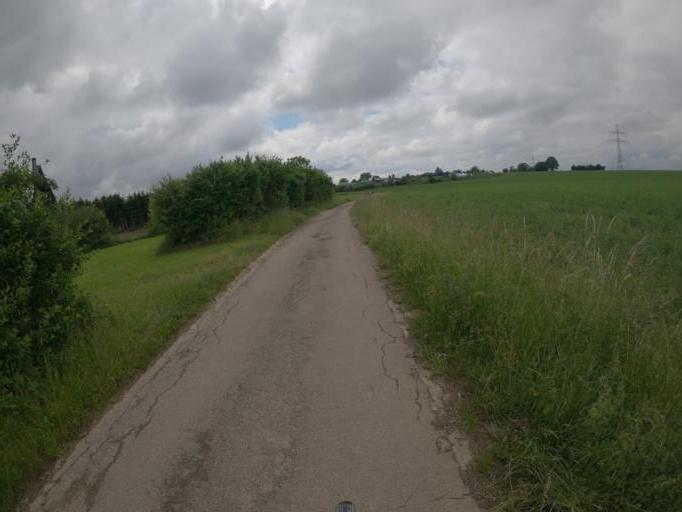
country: DE
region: Baden-Wuerttemberg
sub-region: Regierungsbezirk Stuttgart
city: Hattenhofen
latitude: 48.6745
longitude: 9.5807
